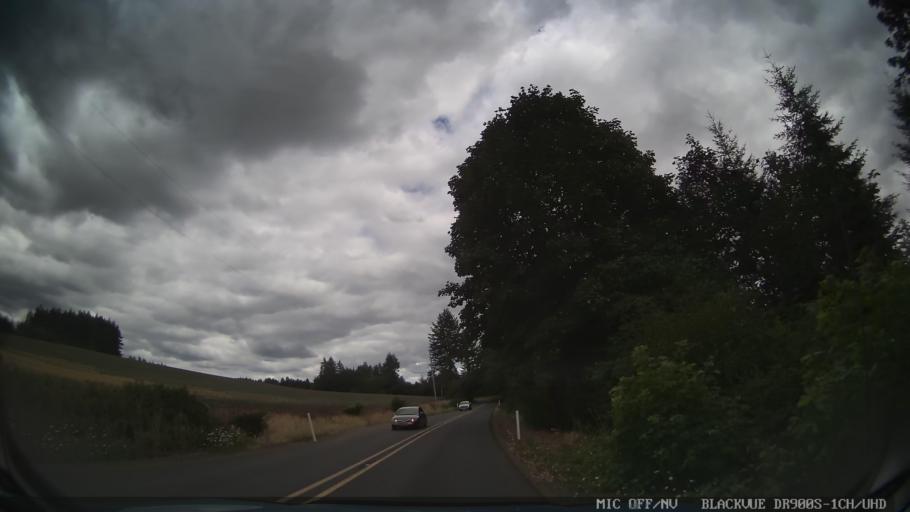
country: US
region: Oregon
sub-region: Linn County
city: Lyons
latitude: 44.8505
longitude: -122.6760
